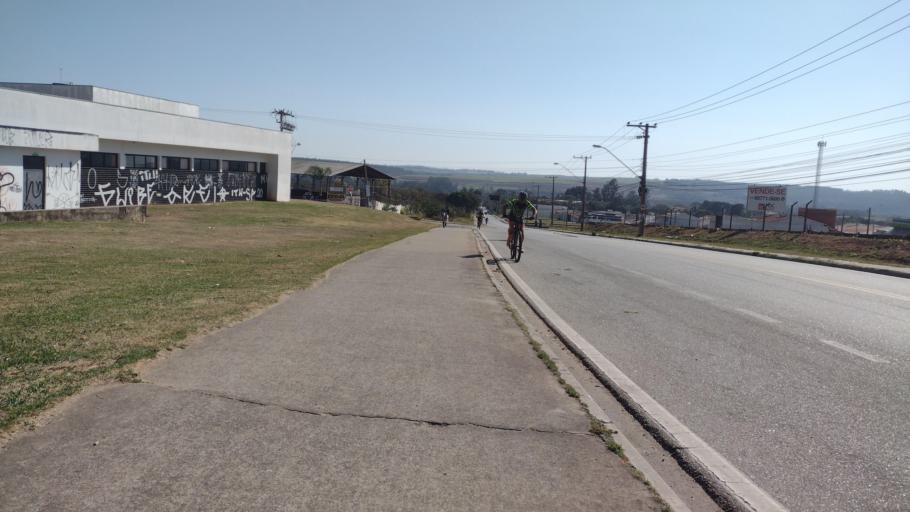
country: BR
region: Sao Paulo
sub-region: Sorocaba
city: Sorocaba
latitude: -23.4225
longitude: -47.4819
